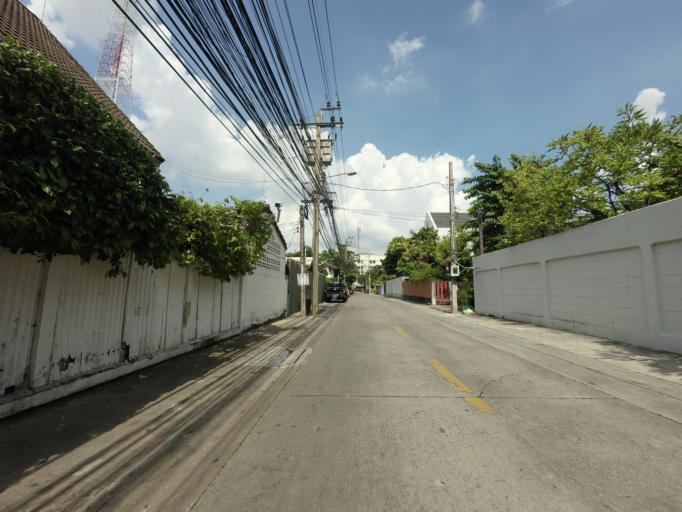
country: TH
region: Bangkok
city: Phaya Thai
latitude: 13.7827
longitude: 100.5519
